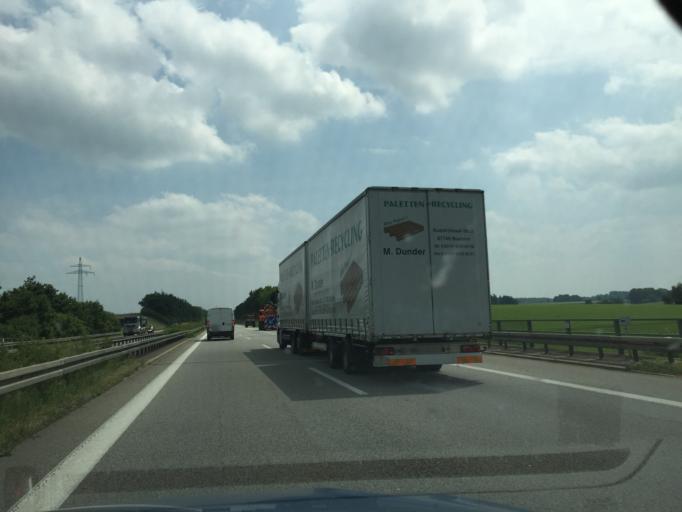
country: DE
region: Bavaria
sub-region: Swabia
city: Holzheim
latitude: 48.3475
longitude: 10.0843
